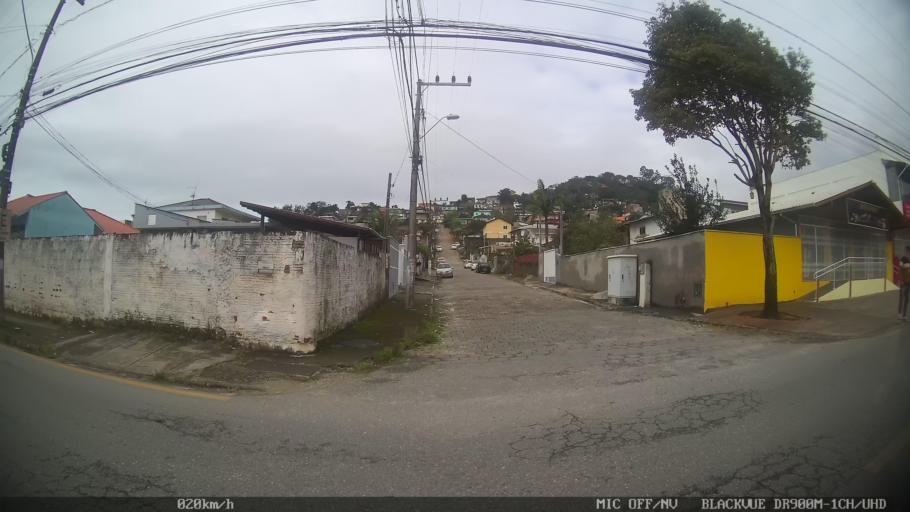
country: BR
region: Santa Catarina
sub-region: Biguacu
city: Biguacu
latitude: -27.5454
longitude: -48.6414
